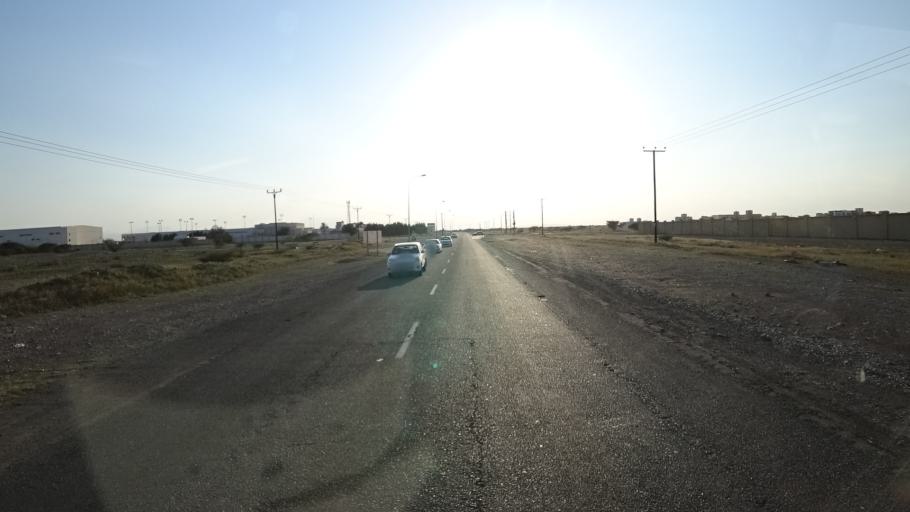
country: OM
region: Al Batinah
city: Al Khaburah
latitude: 23.9485
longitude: 57.0540
